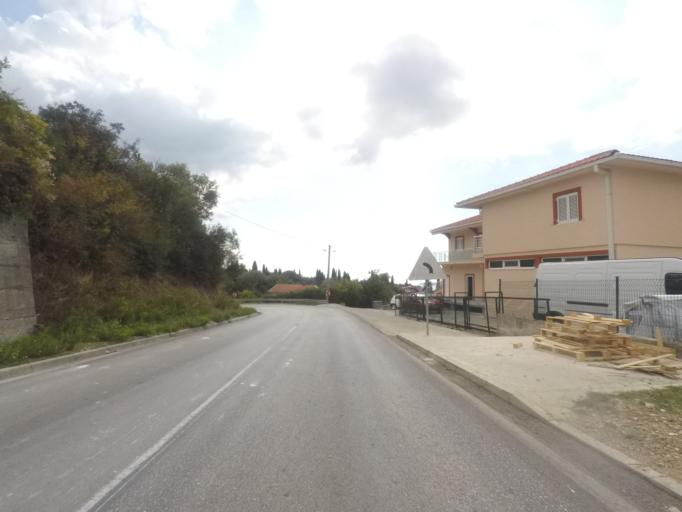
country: ME
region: Herceg Novi
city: Herceg-Novi
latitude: 42.4639
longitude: 18.5457
